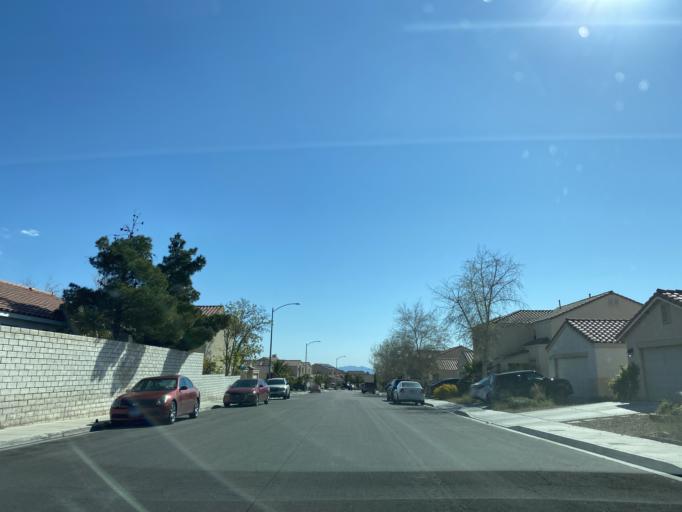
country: US
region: Nevada
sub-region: Clark County
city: Summerlin South
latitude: 36.3046
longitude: -115.2834
